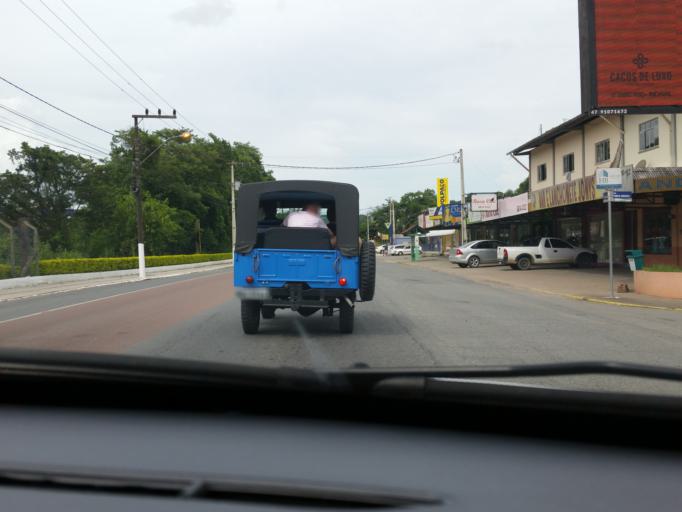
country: BR
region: Santa Catarina
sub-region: Rodeio
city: Gavea
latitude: -27.0357
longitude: -49.3902
